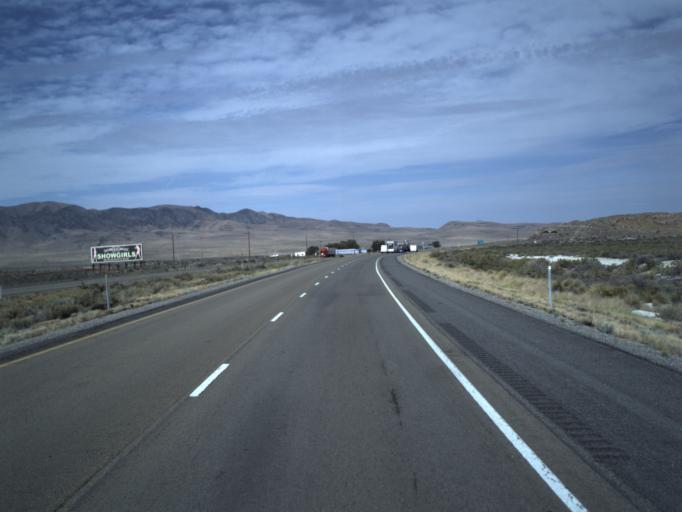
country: US
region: Utah
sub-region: Tooele County
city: Grantsville
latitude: 40.7581
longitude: -112.7701
